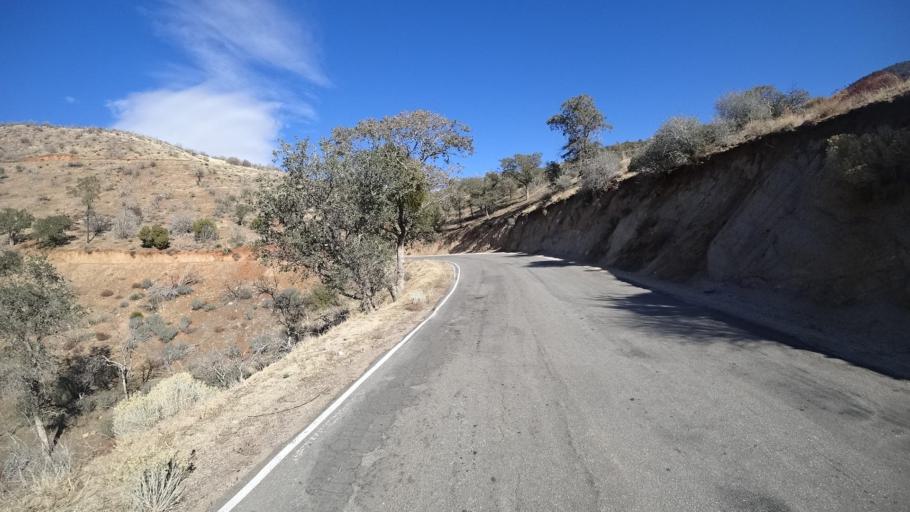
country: US
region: California
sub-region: Kern County
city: Bodfish
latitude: 35.5653
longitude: -118.5044
